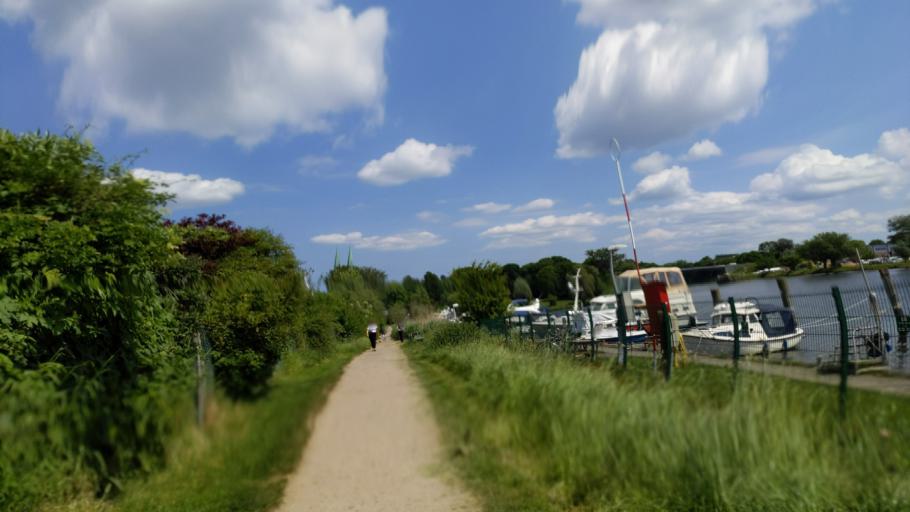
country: DE
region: Schleswig-Holstein
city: Luebeck
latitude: 53.8541
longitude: 10.6747
